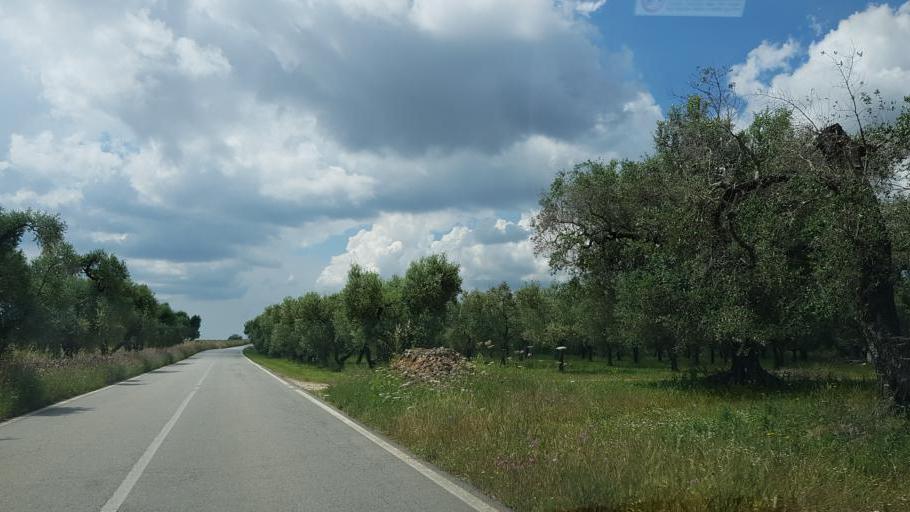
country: IT
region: Apulia
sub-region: Provincia di Brindisi
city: Mesagne
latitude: 40.5124
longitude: 17.8267
